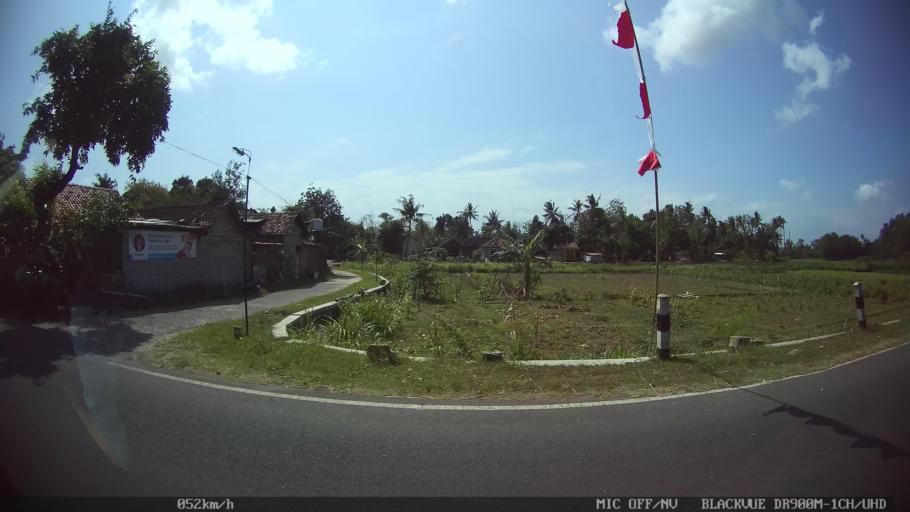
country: ID
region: Daerah Istimewa Yogyakarta
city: Pundong
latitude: -7.9879
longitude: 110.3211
